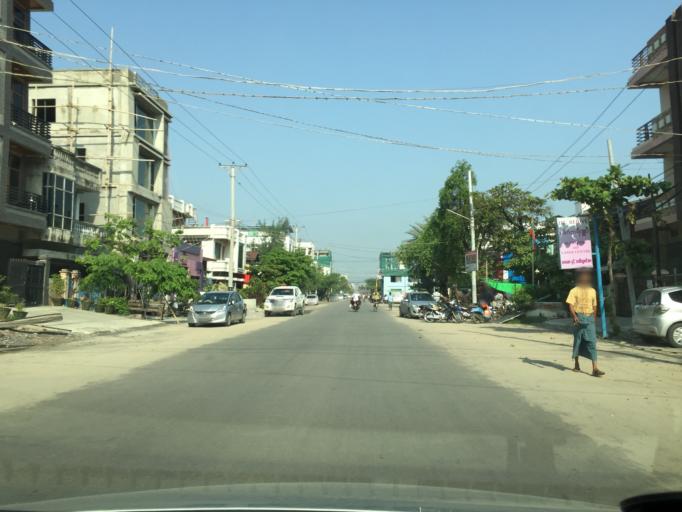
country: MM
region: Mandalay
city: Mandalay
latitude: 21.9735
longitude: 96.0928
